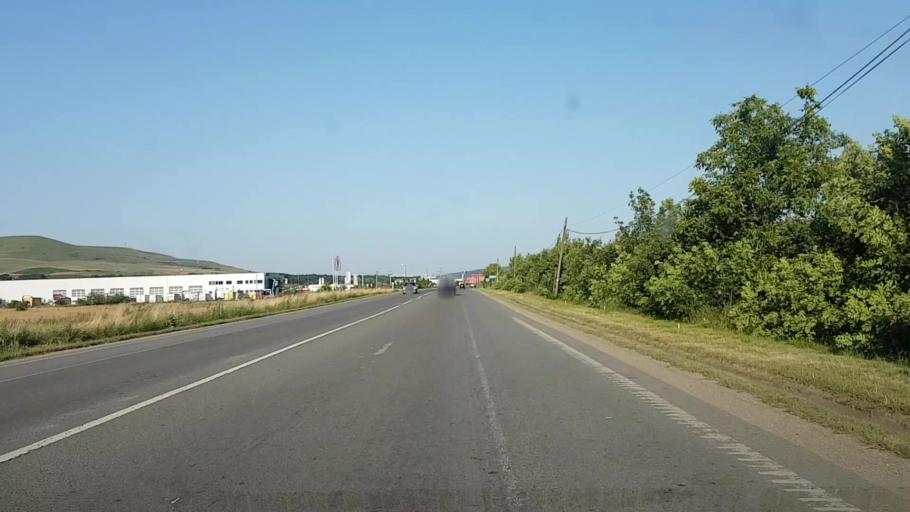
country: RO
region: Cluj
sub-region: Comuna Floresti
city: Luna de Sus
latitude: 46.7507
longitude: 23.4343
